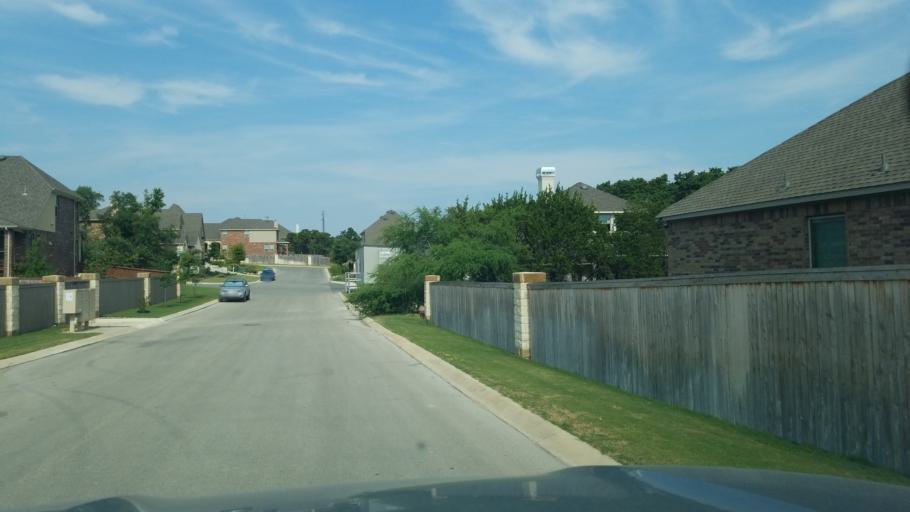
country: US
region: Texas
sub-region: Bexar County
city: Scenic Oaks
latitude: 29.7262
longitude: -98.6619
